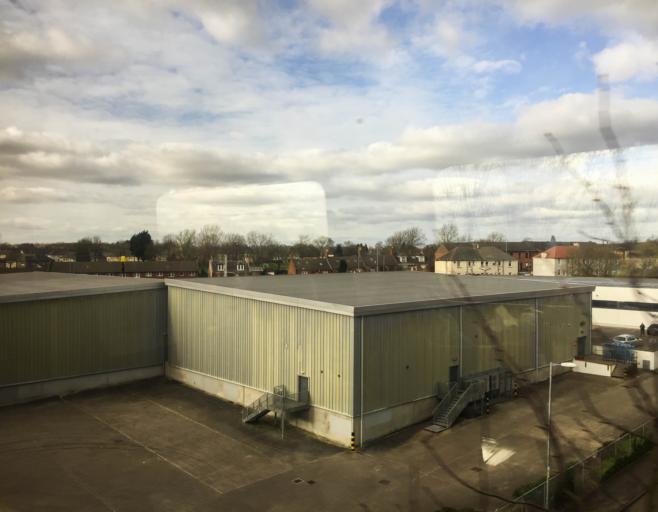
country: GB
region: Scotland
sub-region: North Lanarkshire
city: Wishaw
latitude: 55.7742
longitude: -3.9316
